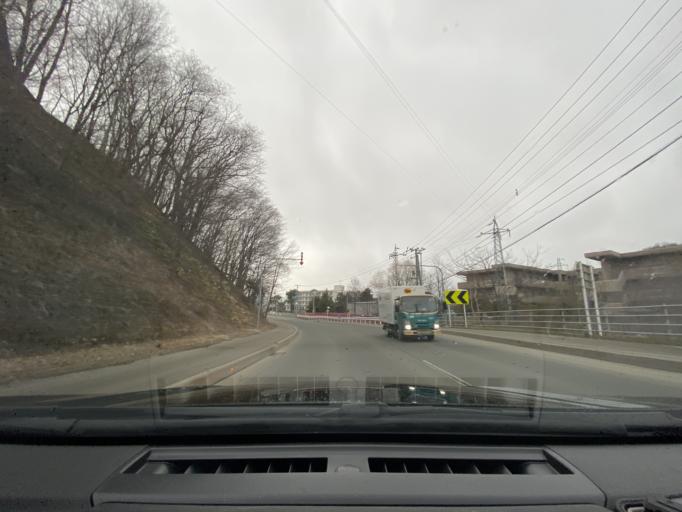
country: JP
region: Hokkaido
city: Kitami
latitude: 43.7966
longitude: 143.9167
